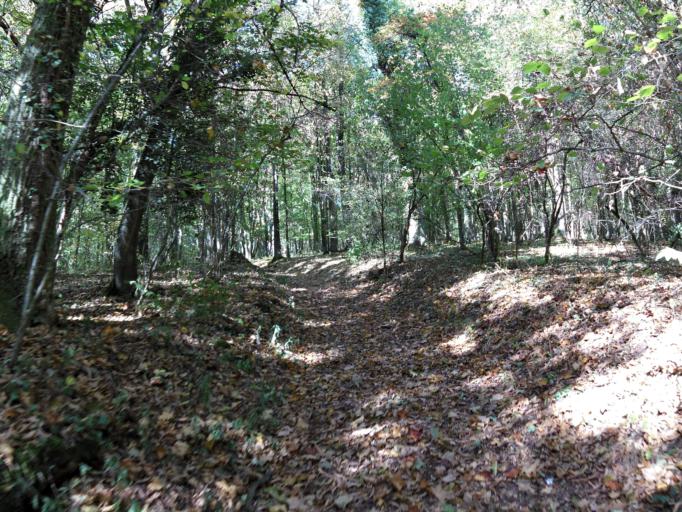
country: DE
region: Bavaria
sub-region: Regierungsbezirk Unterfranken
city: Eibelstadt
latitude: 49.7231
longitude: 9.9827
